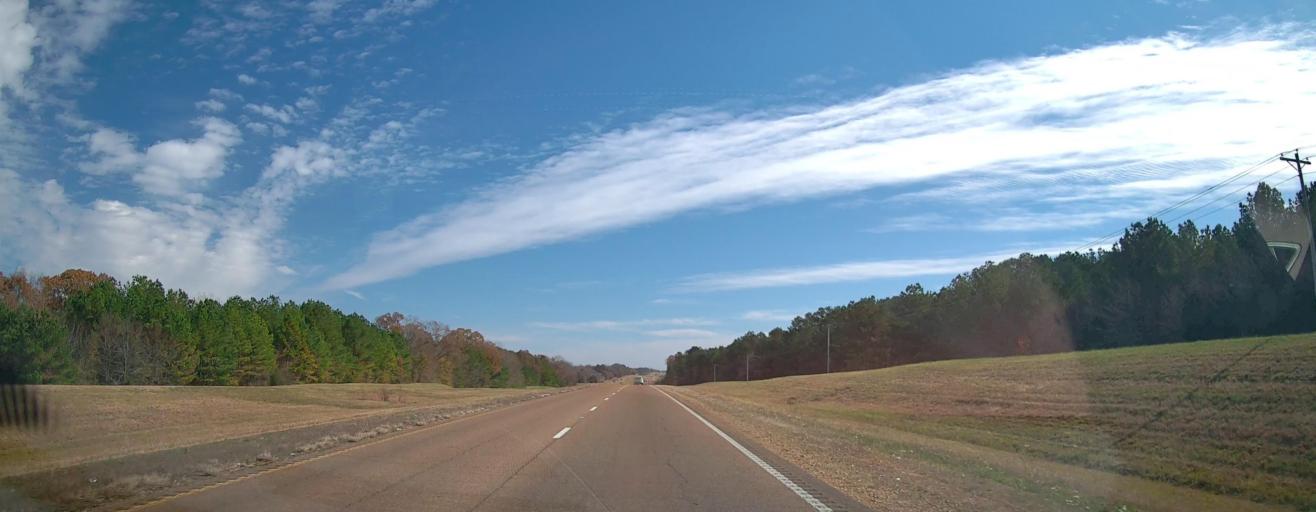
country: US
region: Tennessee
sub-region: Fayette County
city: Piperton
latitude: 34.9561
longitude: -89.5014
